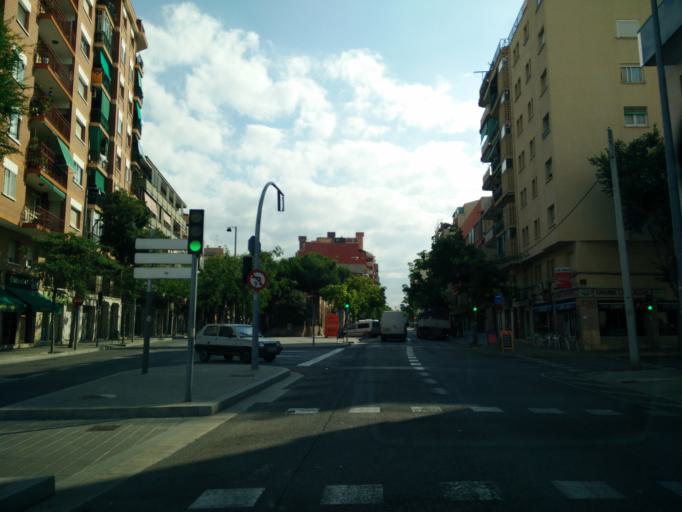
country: ES
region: Catalonia
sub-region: Provincia de Barcelona
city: Llefia
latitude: 41.4421
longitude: 2.2334
